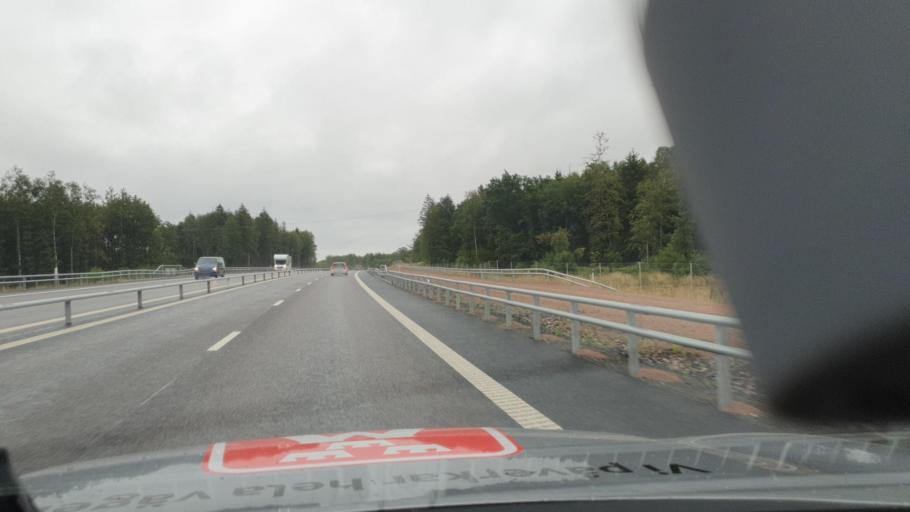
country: SE
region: Skane
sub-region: Hassleholms Kommun
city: Vinslov
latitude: 55.9455
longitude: 13.8763
